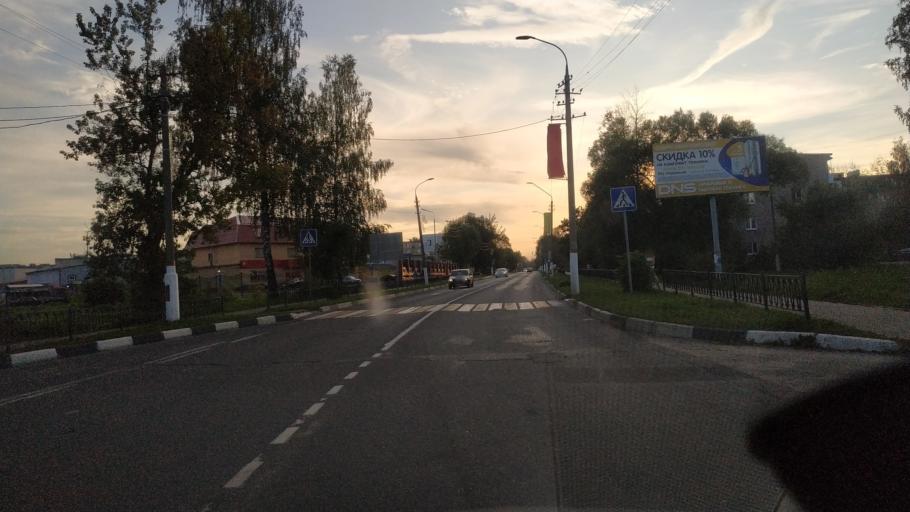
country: RU
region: Moskovskaya
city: Roshal'
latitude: 55.6633
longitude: 39.8575
